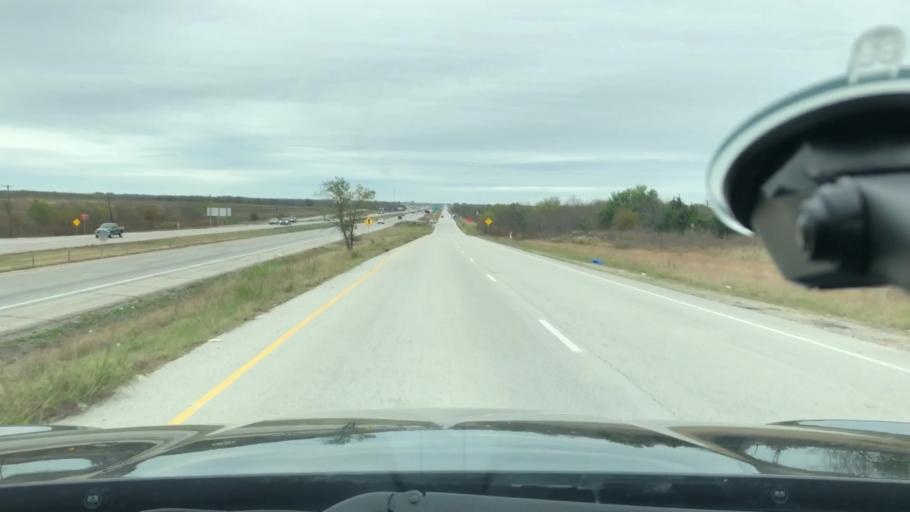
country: US
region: Texas
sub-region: Kaufman County
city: Talty
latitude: 32.7396
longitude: -96.3945
